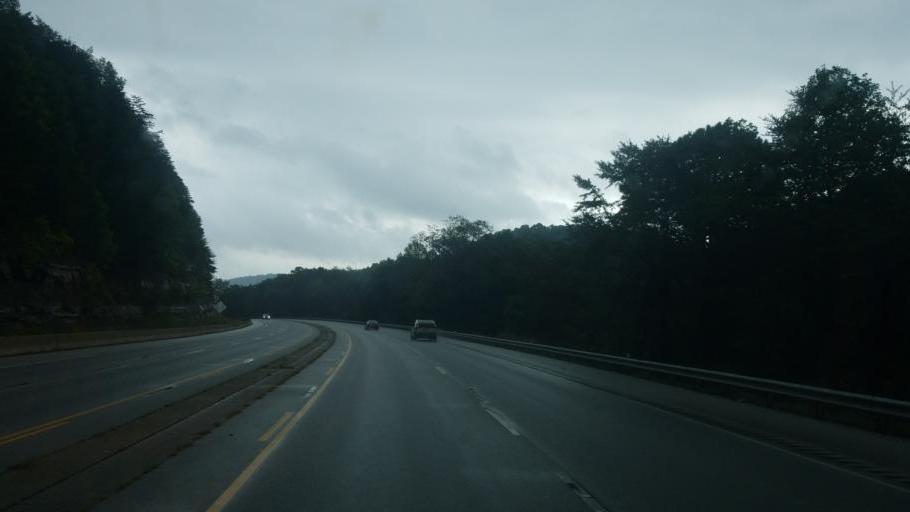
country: US
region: Kentucky
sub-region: Rowan County
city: Morehead
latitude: 38.1791
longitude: -83.4600
